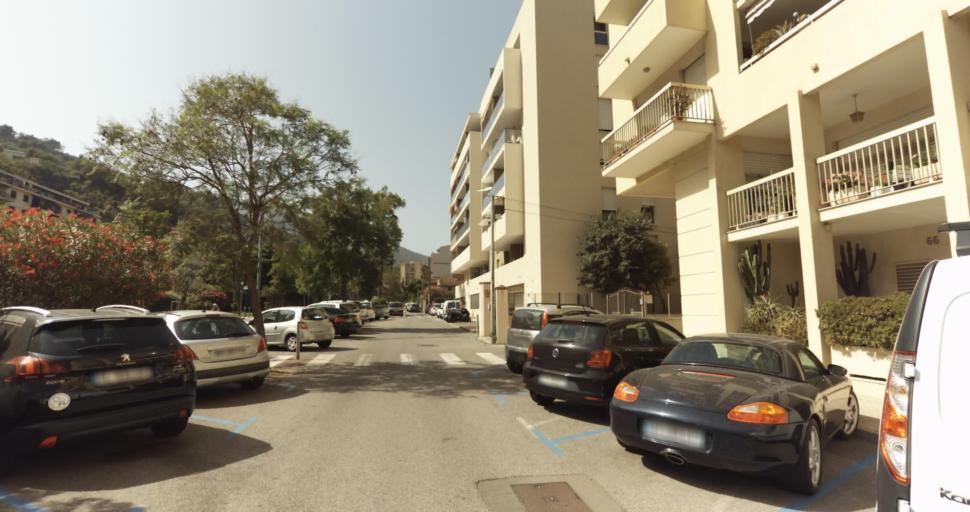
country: FR
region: Provence-Alpes-Cote d'Azur
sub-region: Departement des Alpes-Maritimes
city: Menton
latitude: 43.7868
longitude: 7.4940
